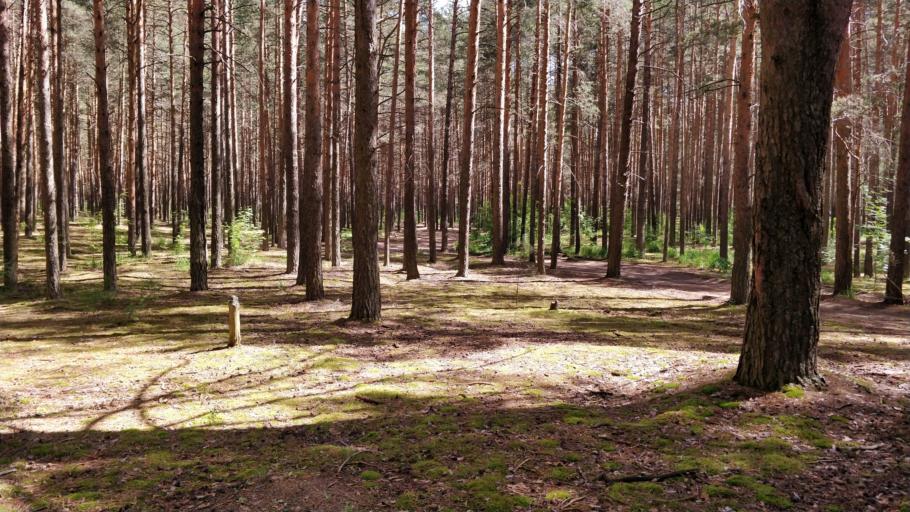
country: RU
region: Perm
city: Perm
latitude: 58.0595
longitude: 56.2880
